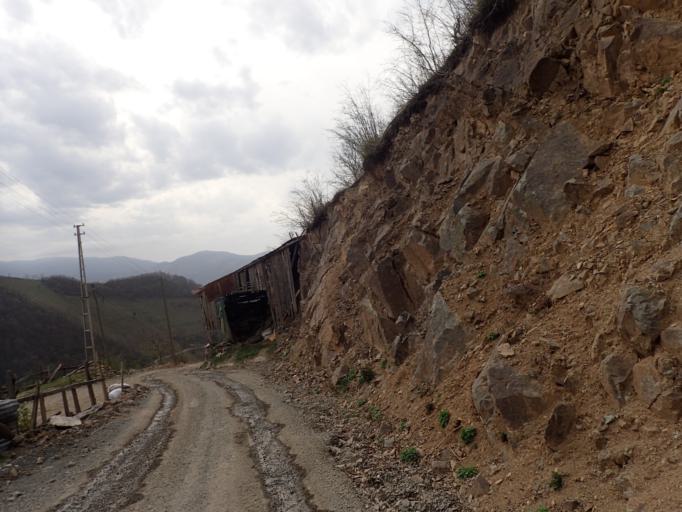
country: TR
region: Ordu
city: Kabaduz
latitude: 40.8161
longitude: 37.8837
